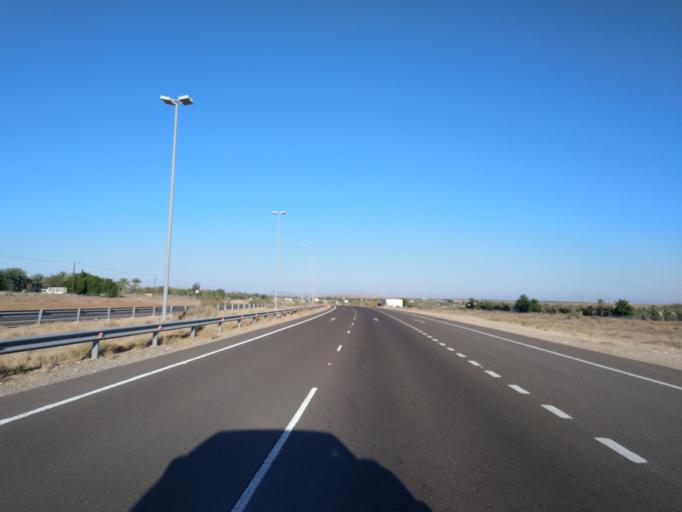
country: OM
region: Al Buraimi
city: Al Buraymi
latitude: 24.5416
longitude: 55.6402
